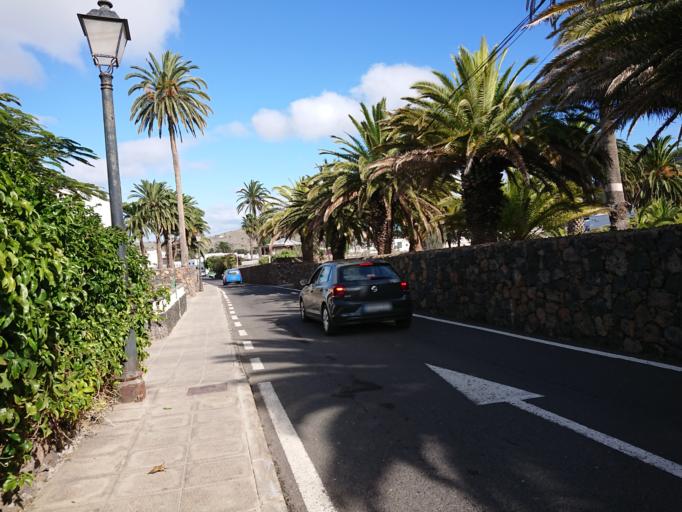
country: ES
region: Canary Islands
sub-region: Provincia de Las Palmas
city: Haria
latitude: 29.1423
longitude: -13.5043
